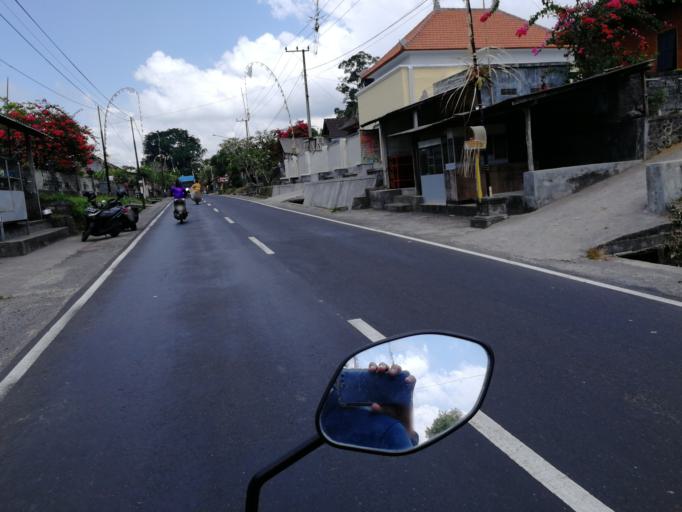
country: ID
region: Bali
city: Banjar Kubu
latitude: -8.4286
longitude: 115.4213
